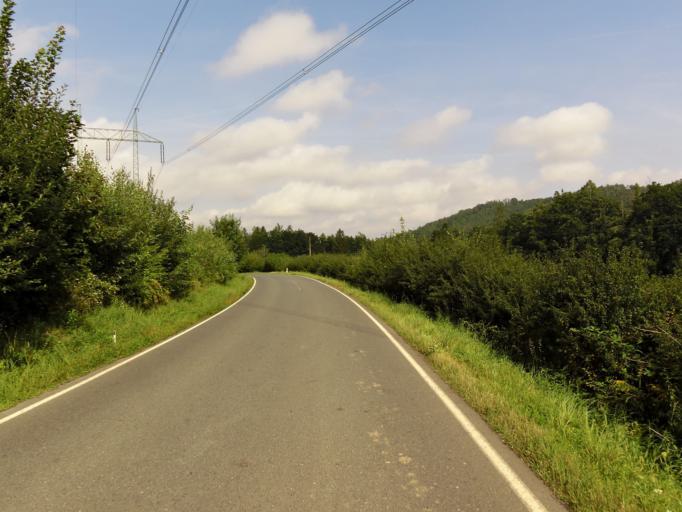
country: CZ
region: Central Bohemia
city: Tynec nad Sazavou
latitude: 49.8592
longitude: 14.5784
